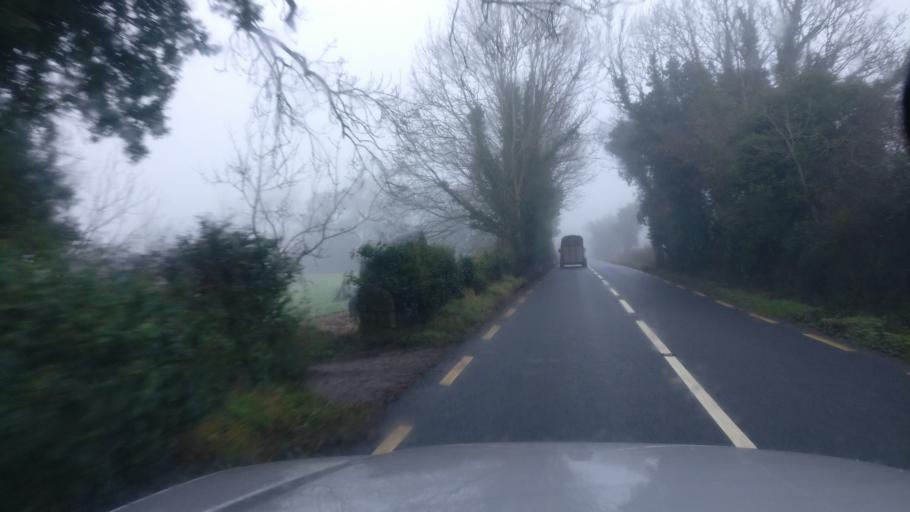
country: IE
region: Connaught
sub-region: County Galway
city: Loughrea
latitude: 53.1545
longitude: -8.6909
